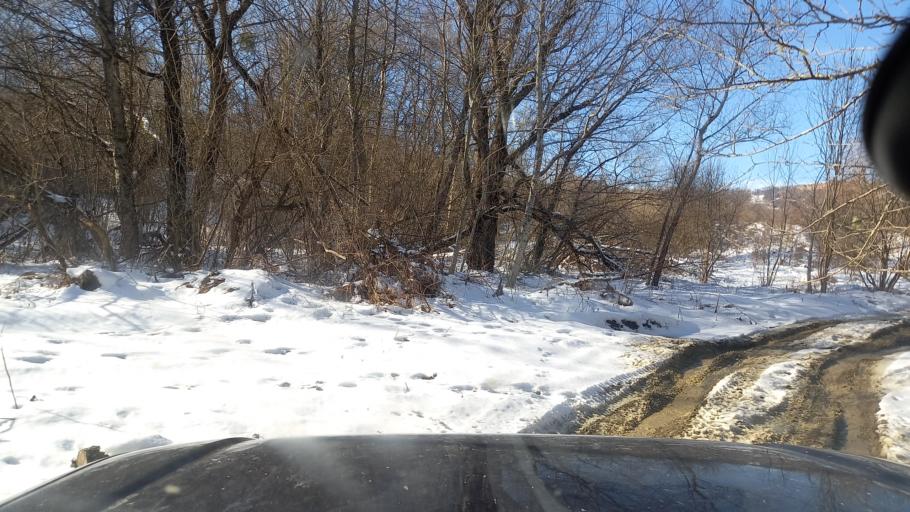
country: RU
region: Adygeya
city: Kamennomostskiy
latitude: 44.2073
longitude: 40.1465
